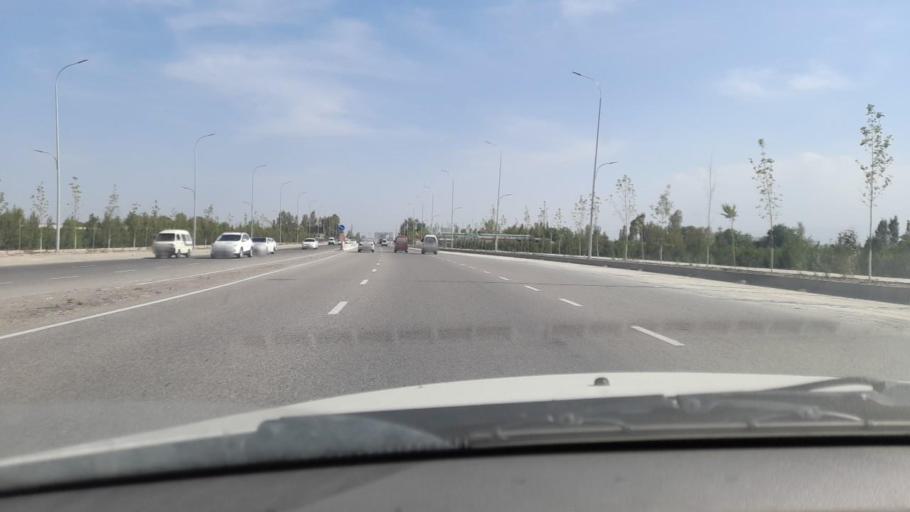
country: UZ
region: Samarqand
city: Daxbet
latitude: 39.7482
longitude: 66.9221
